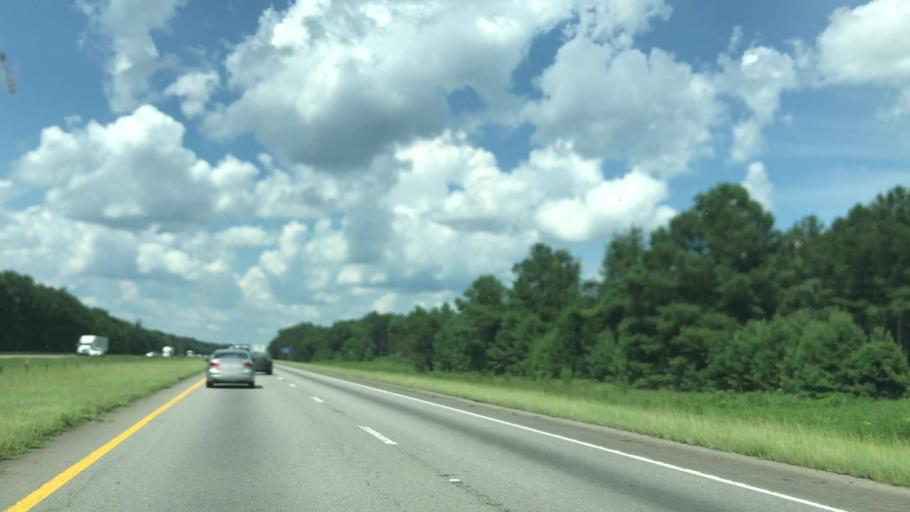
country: US
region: South Carolina
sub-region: Hampton County
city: Yemassee
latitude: 32.6090
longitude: -80.8958
